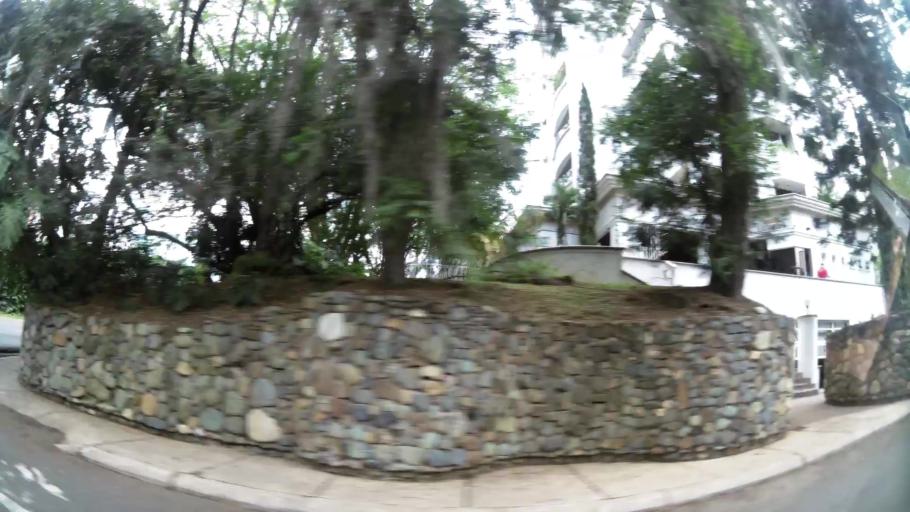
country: CO
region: Antioquia
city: Envigado
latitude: 6.1891
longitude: -75.5759
